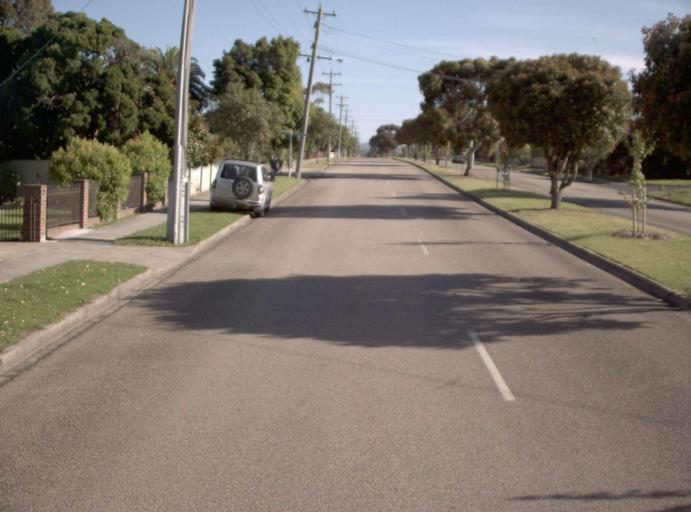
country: AU
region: Victoria
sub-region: East Gippsland
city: Lakes Entrance
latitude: -37.7019
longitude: 148.4561
